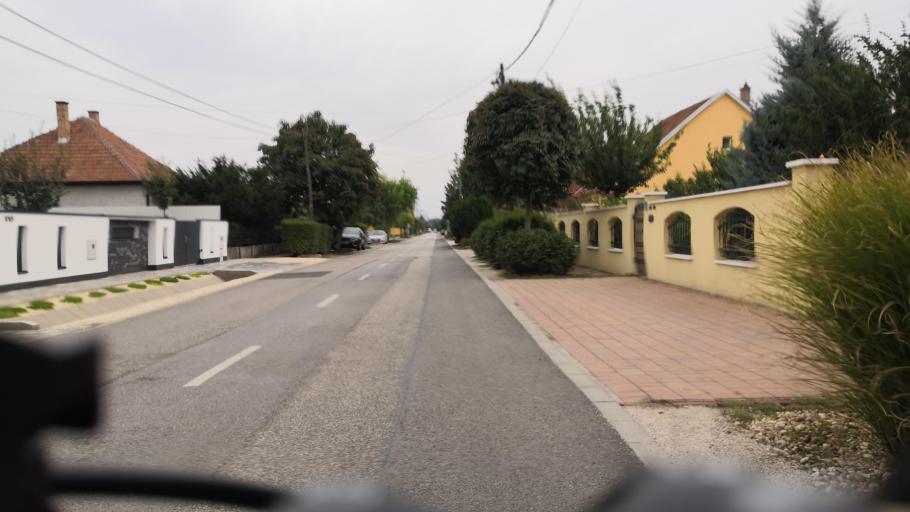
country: HU
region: Csongrad
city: Szeged
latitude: 46.2895
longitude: 20.1635
